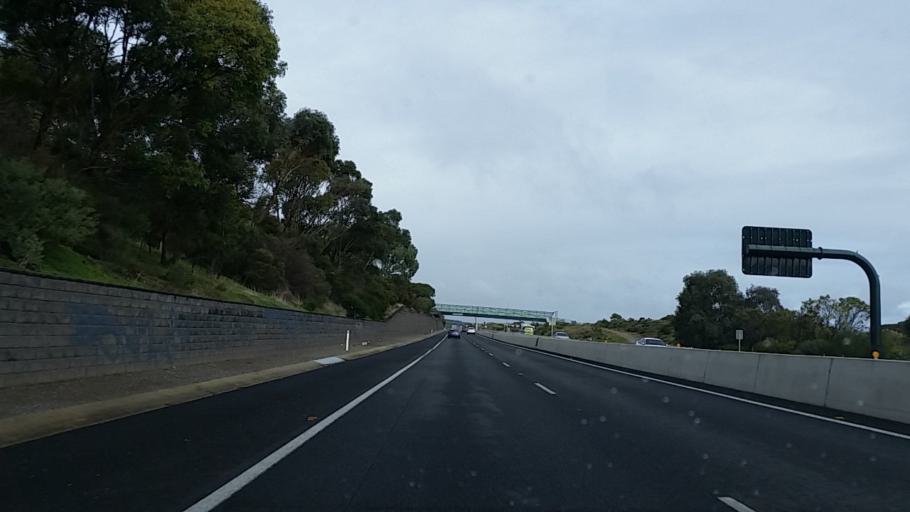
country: AU
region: South Australia
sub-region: Onkaparinga
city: Noarlunga Downs
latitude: -35.1496
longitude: 138.5058
